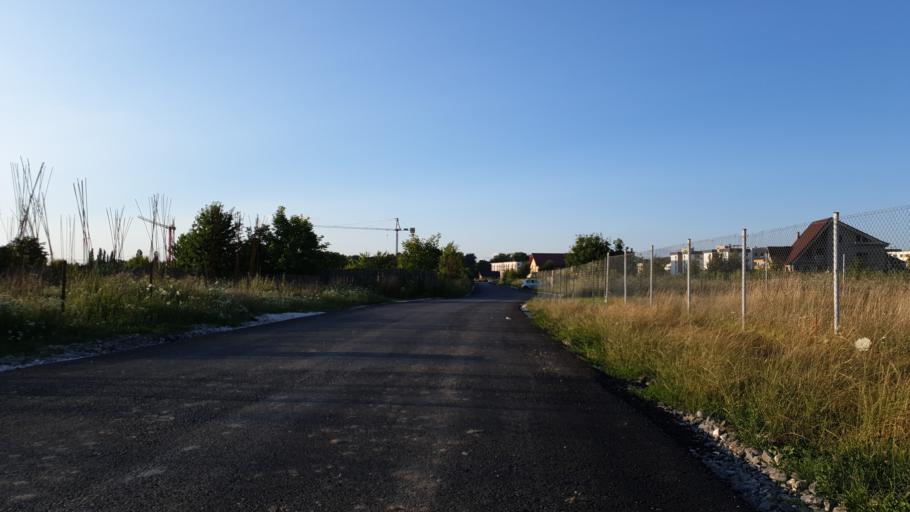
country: RO
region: Brasov
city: Brasov
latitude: 45.6769
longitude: 25.6048
